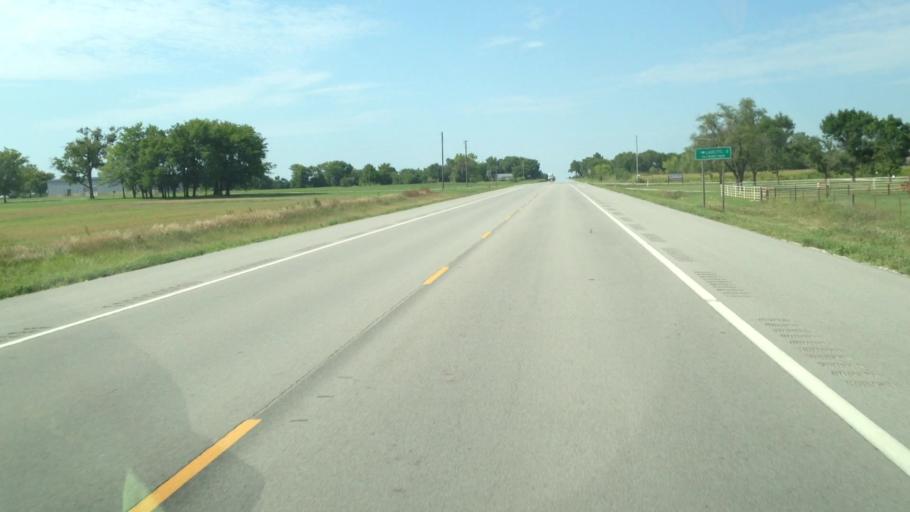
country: US
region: Kansas
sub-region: Labette County
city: Altamont
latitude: 37.2502
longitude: -95.2670
